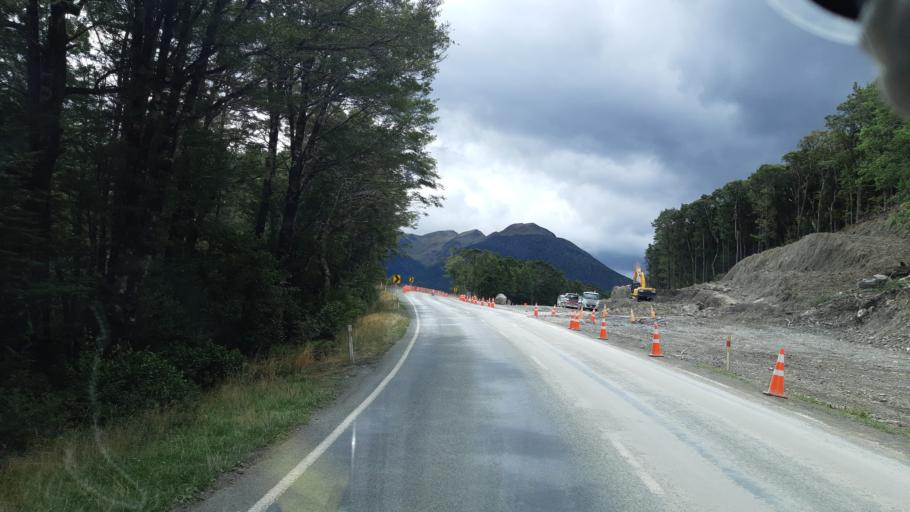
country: NZ
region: Canterbury
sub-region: Hurunui District
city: Amberley
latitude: -42.4920
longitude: 172.3877
